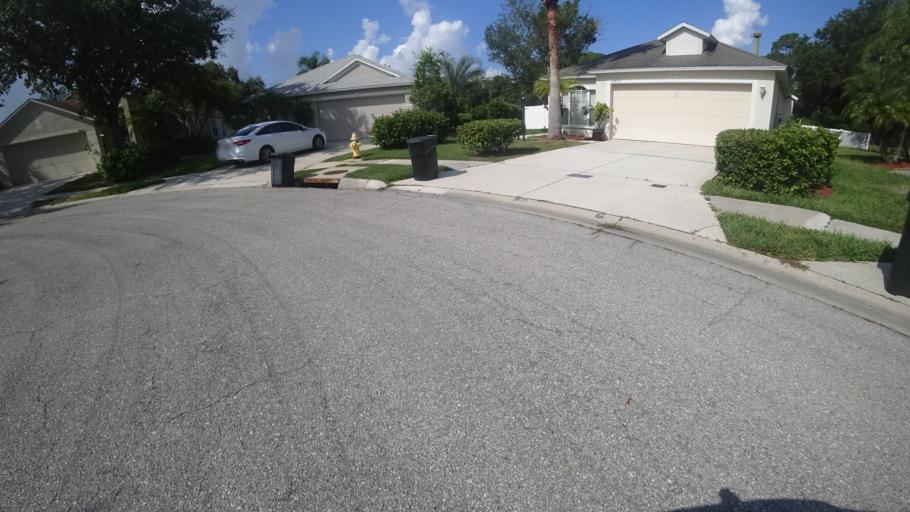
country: US
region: Florida
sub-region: Sarasota County
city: The Meadows
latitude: 27.4310
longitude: -82.4241
